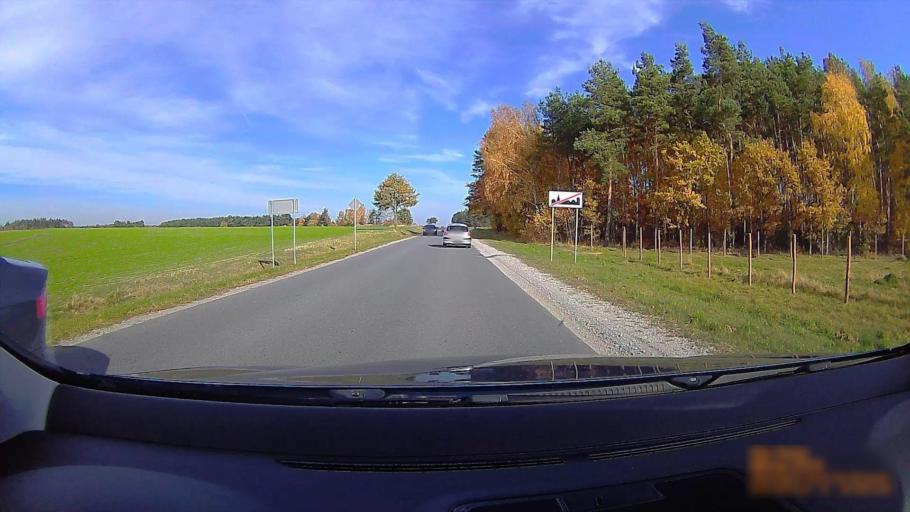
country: PL
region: Greater Poland Voivodeship
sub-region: Powiat ostrzeszowski
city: Doruchow
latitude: 51.3706
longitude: 18.0345
